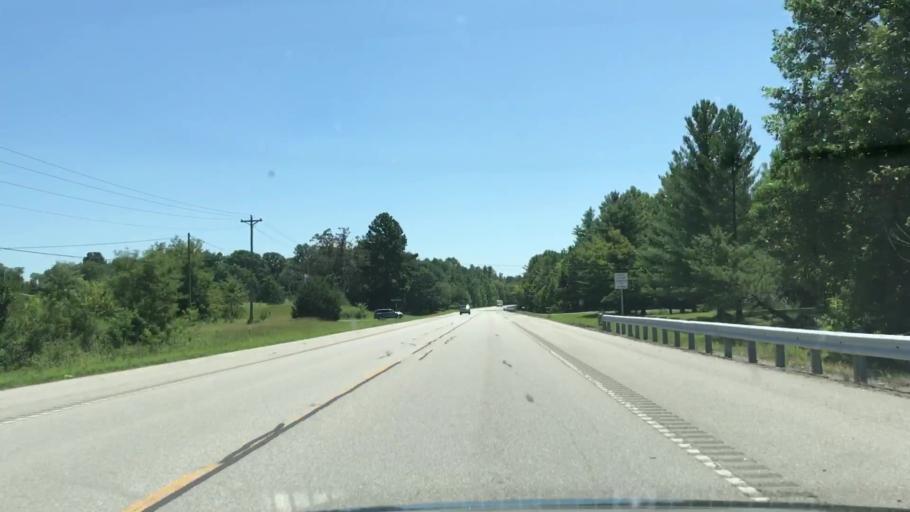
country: US
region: Tennessee
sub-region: Putnam County
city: Baxter
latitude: 36.2136
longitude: -85.6132
